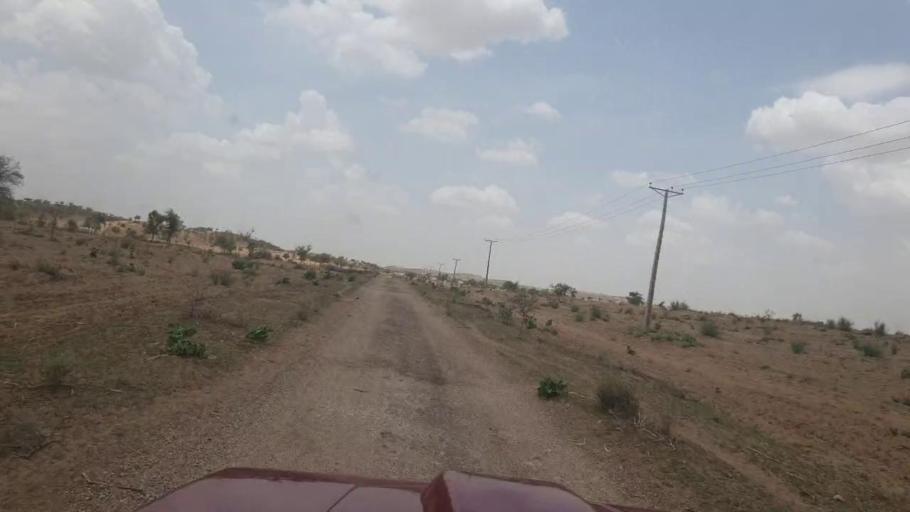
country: PK
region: Sindh
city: Islamkot
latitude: 25.2070
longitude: 70.4495
